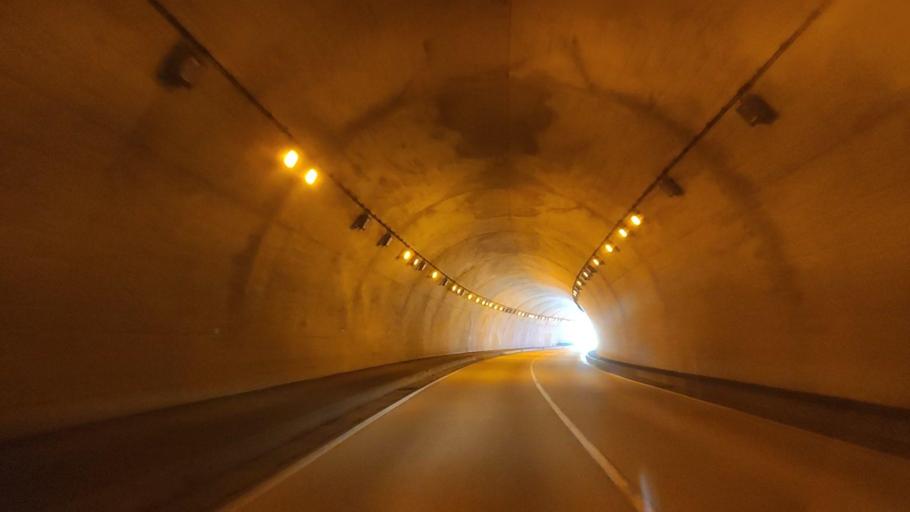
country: JP
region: Ishikawa
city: Nanao
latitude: 37.3827
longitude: 137.2338
